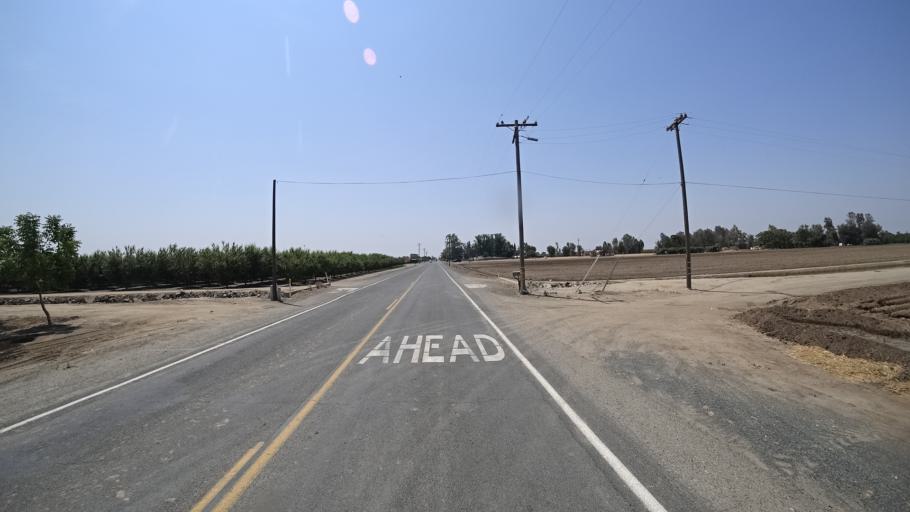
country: US
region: California
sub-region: Kings County
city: Lemoore
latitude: 36.3444
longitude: -119.7808
